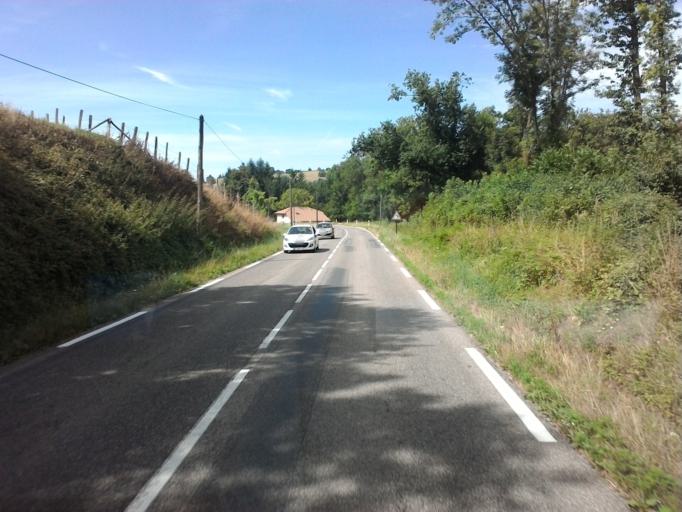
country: FR
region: Rhone-Alpes
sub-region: Departement de l'Isere
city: Montferrat
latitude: 45.4931
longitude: 5.5759
